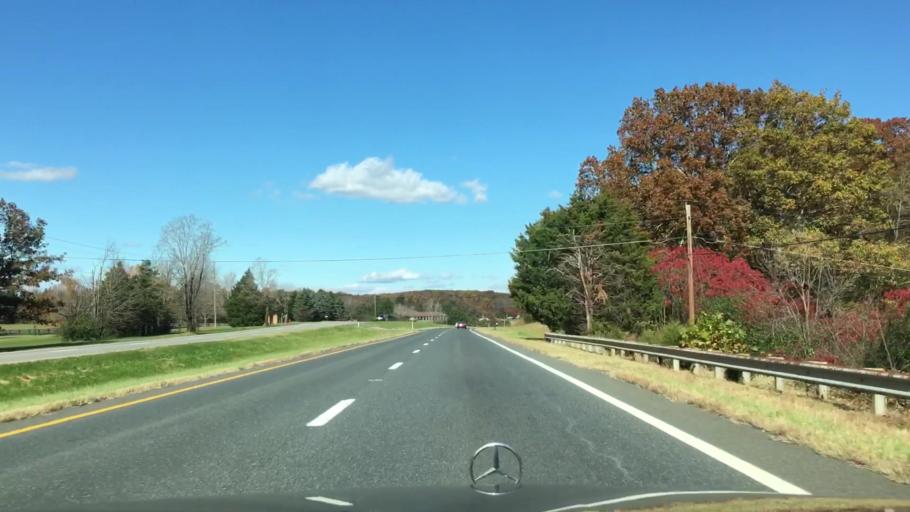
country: US
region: Virginia
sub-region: Campbell County
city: Rustburg
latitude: 37.2442
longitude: -79.1876
